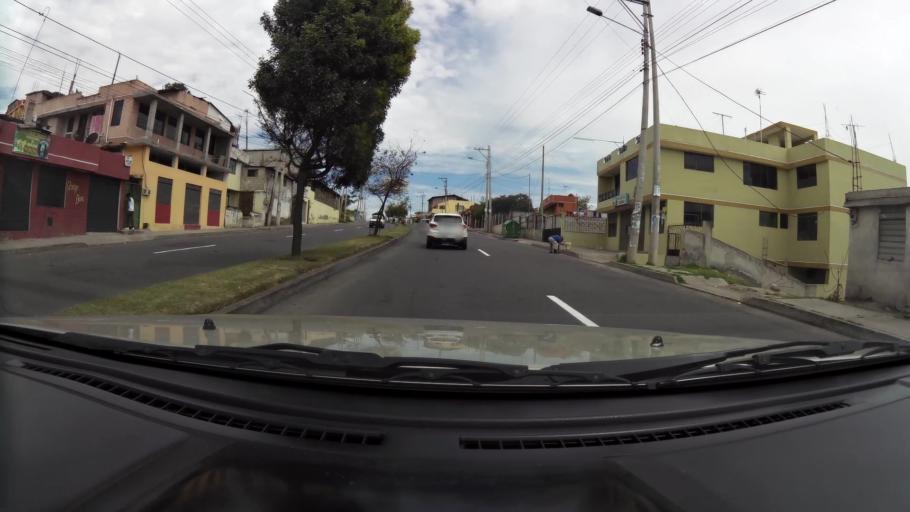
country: EC
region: Tungurahua
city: Pillaro
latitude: -1.1239
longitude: -78.5890
